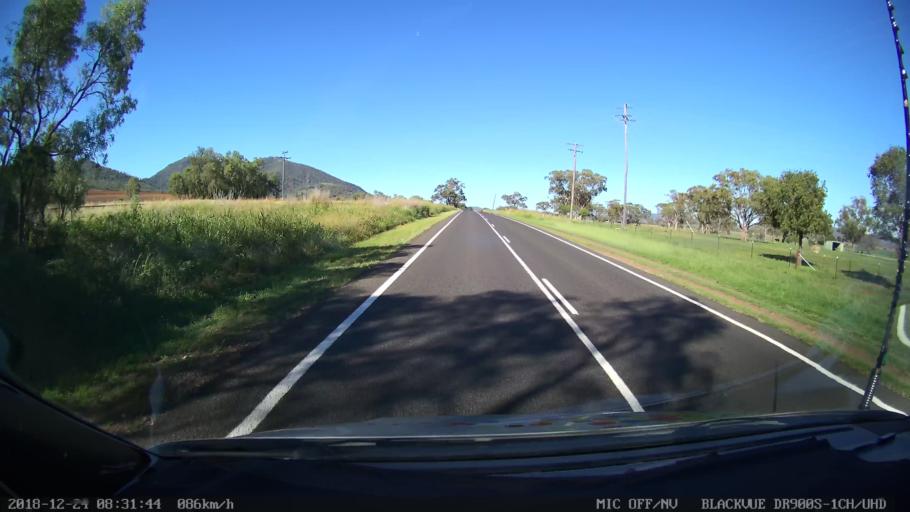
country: AU
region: New South Wales
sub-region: Tamworth Municipality
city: Phillip
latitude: -31.2754
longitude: 150.7076
